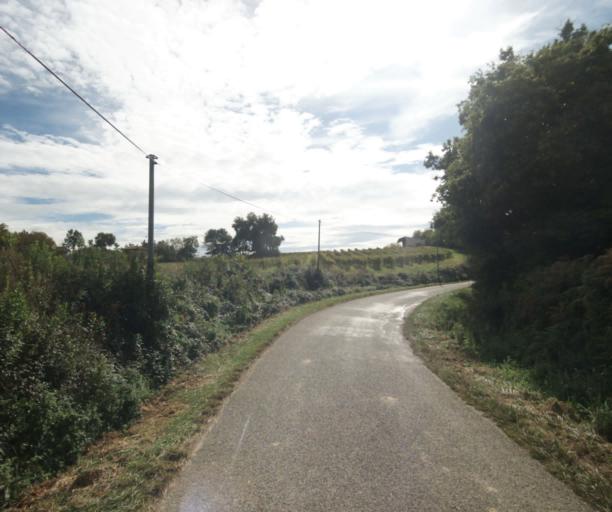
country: FR
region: Aquitaine
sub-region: Departement des Landes
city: Villeneuve-de-Marsan
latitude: 43.8962
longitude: -0.1955
